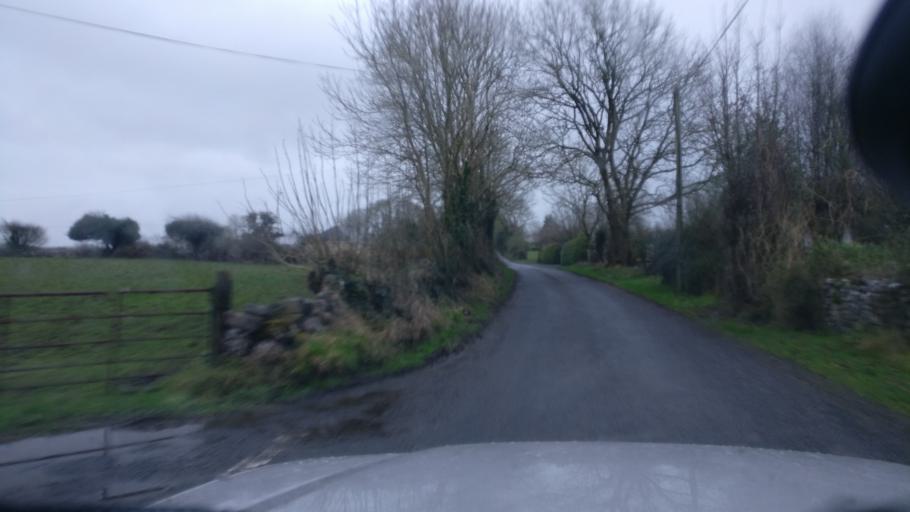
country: IE
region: Connaught
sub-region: County Galway
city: Loughrea
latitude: 53.2174
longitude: -8.5902
